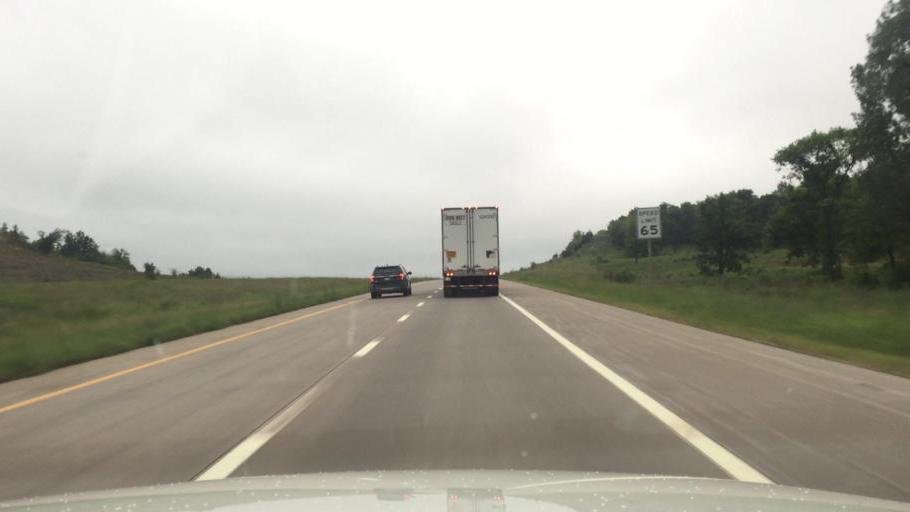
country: US
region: Kansas
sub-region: Montgomery County
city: Cherryvale
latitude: 37.2167
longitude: -95.5855
